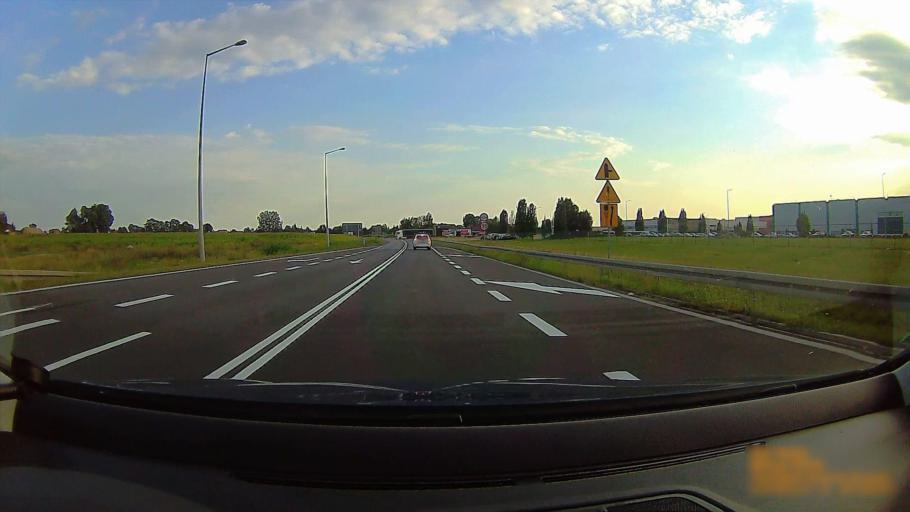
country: PL
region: Greater Poland Voivodeship
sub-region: Powiat koninski
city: Stare Miasto
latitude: 52.1604
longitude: 18.2059
